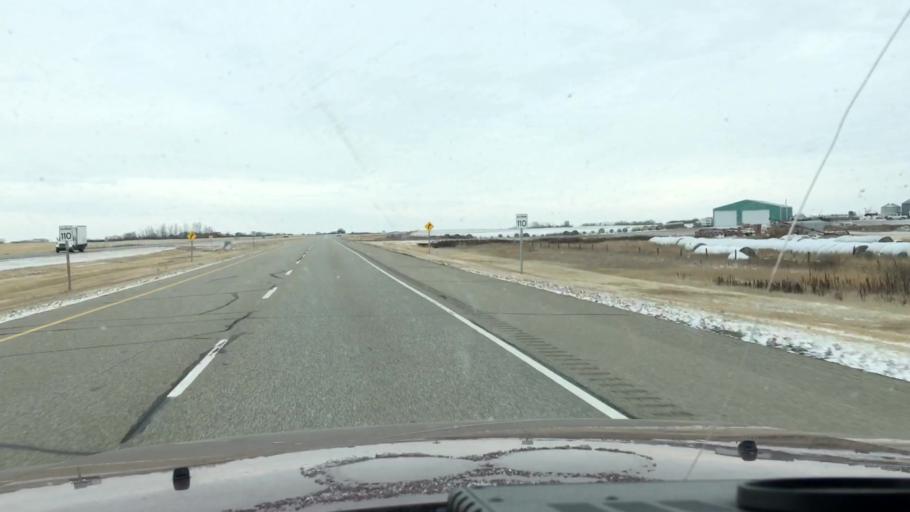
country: CA
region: Saskatchewan
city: Watrous
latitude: 51.3666
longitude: -106.1327
